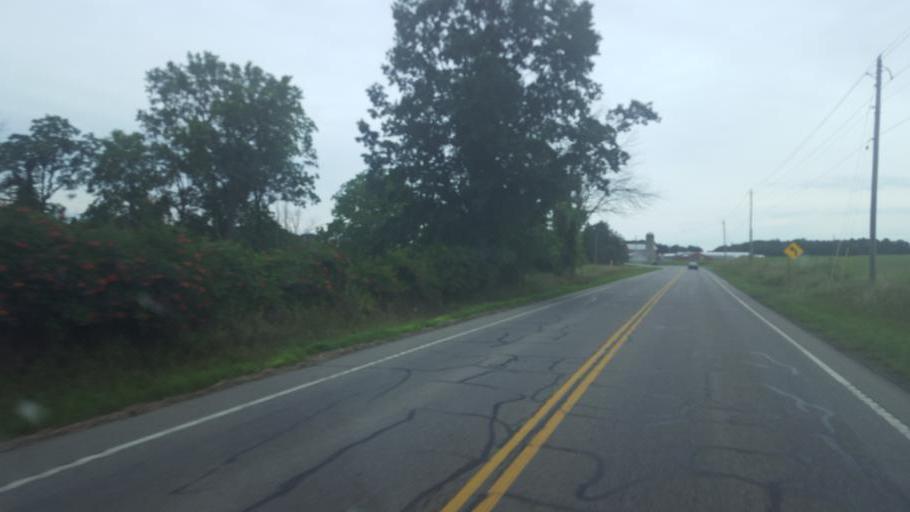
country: US
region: Ohio
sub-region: Richland County
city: Lincoln Heights
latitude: 40.9002
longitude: -82.5018
